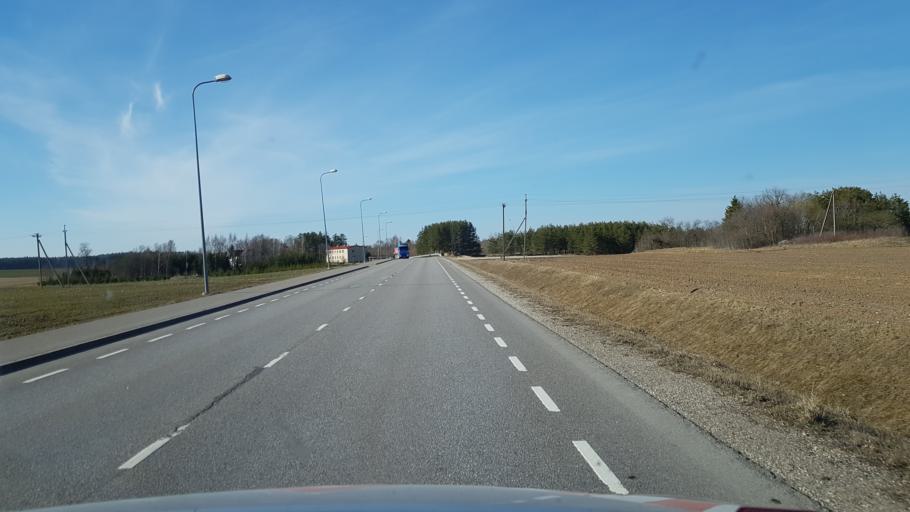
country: EE
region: Laeaene-Virumaa
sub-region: Vinni vald
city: Vinni
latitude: 59.1518
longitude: 26.5927
